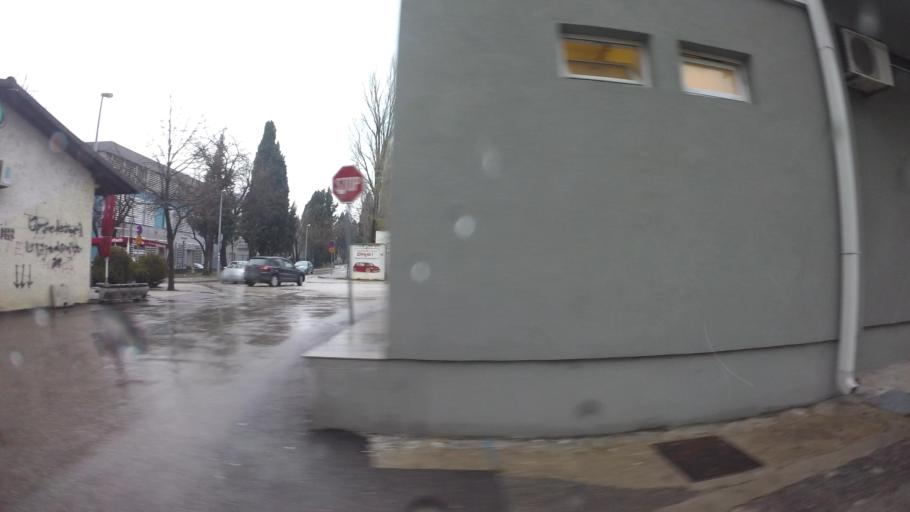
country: BA
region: Federation of Bosnia and Herzegovina
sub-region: Hercegovacko-Bosanski Kanton
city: Mostar
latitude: 43.3475
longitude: 17.7963
